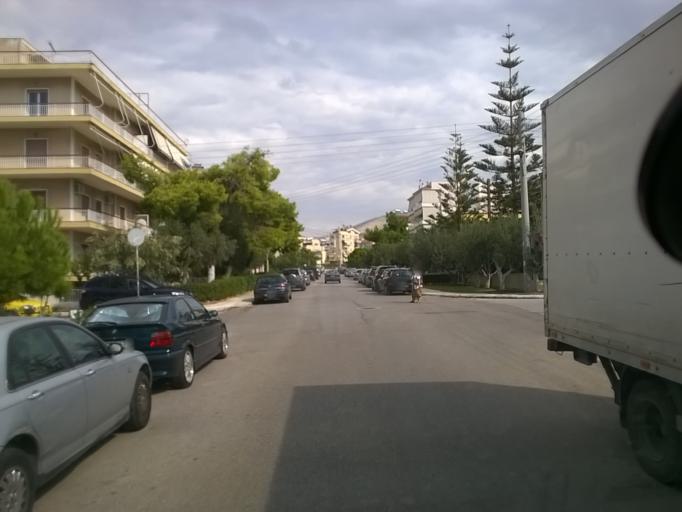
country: GR
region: Attica
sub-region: Nomarchia Athinas
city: Glyfada
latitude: 37.8828
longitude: 23.7575
